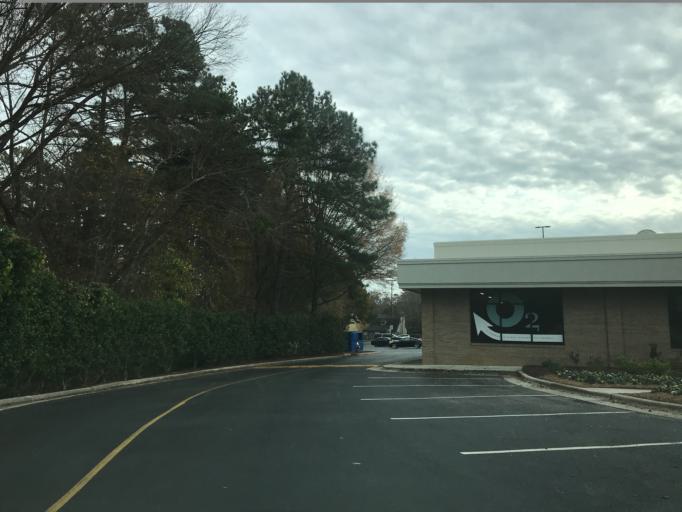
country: US
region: North Carolina
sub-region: Wake County
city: West Raleigh
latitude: 35.8672
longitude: -78.6182
